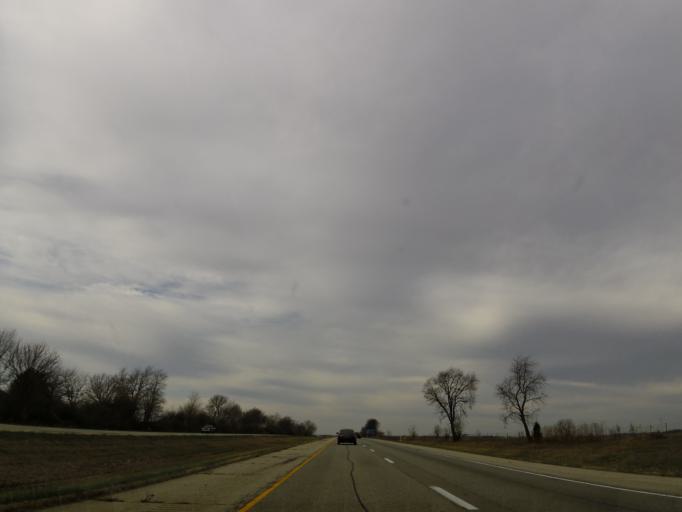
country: US
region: Illinois
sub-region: Peoria County
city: Elmwood
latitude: 40.8140
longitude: -89.8441
